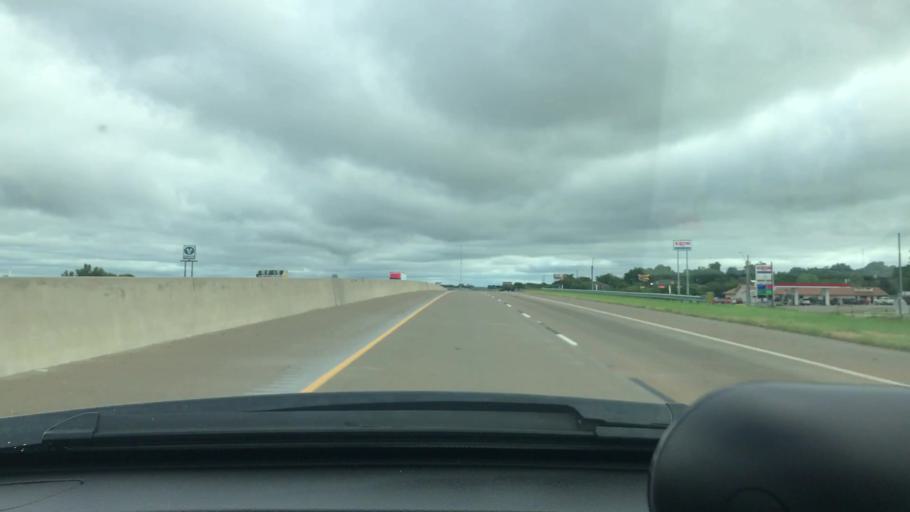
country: US
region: Texas
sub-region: Grayson County
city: Howe
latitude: 33.5053
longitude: -96.6183
